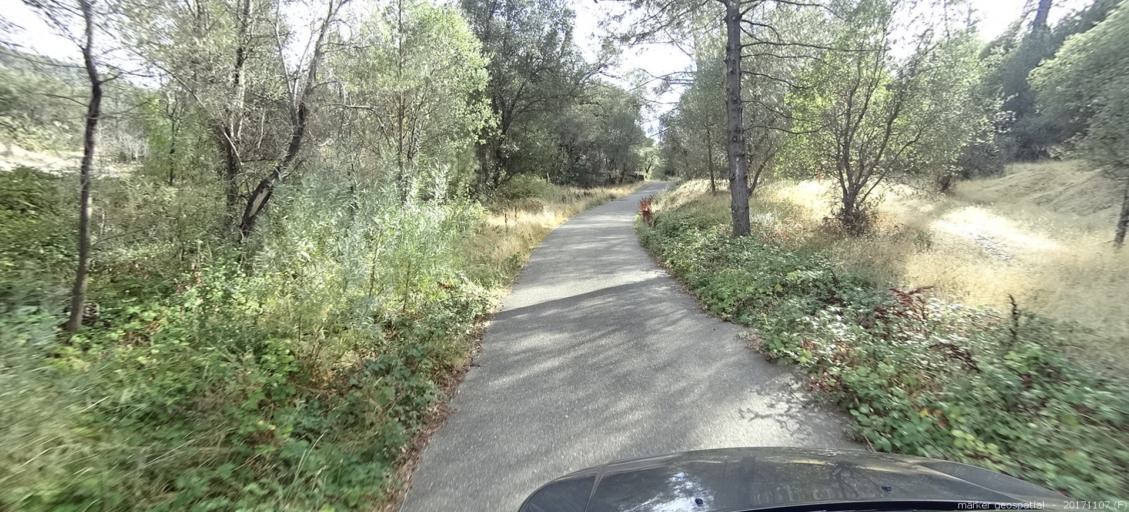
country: US
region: California
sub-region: Shasta County
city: Shasta
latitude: 40.5404
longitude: -122.5266
